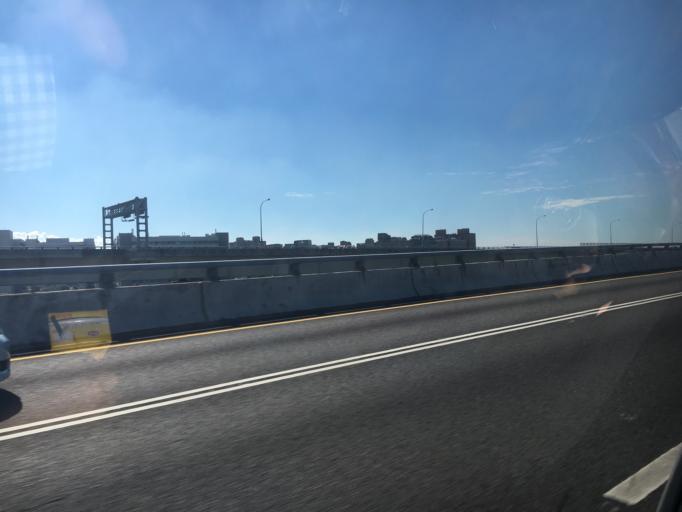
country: TW
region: Taiwan
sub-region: Taoyuan
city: Taoyuan
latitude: 25.0657
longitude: 121.3686
